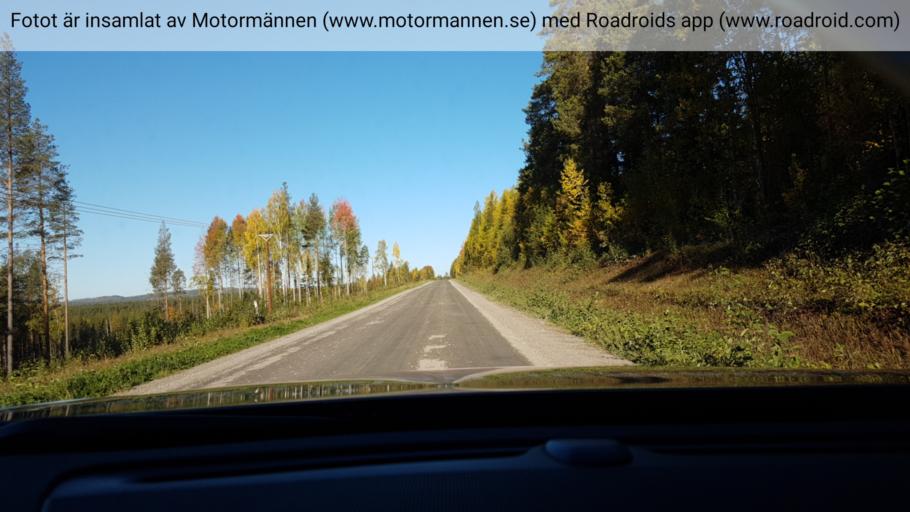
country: SE
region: Norrbotten
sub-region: Alvsbyns Kommun
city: AElvsbyn
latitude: 66.1842
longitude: 21.2143
